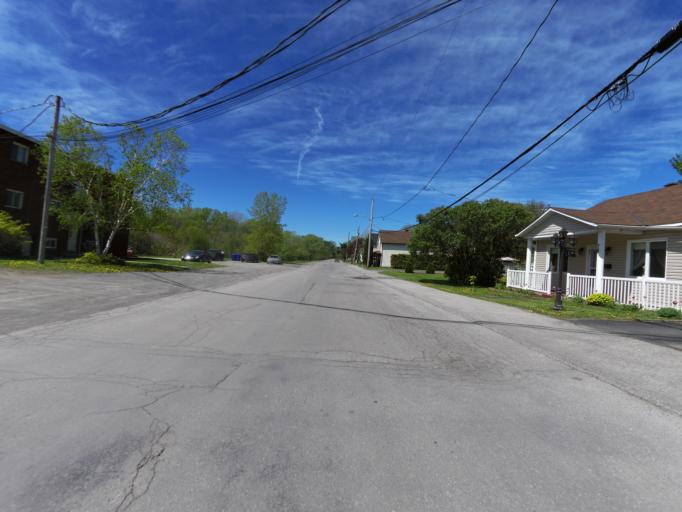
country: CA
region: Ontario
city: Bells Corners
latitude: 45.3813
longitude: -75.8055
